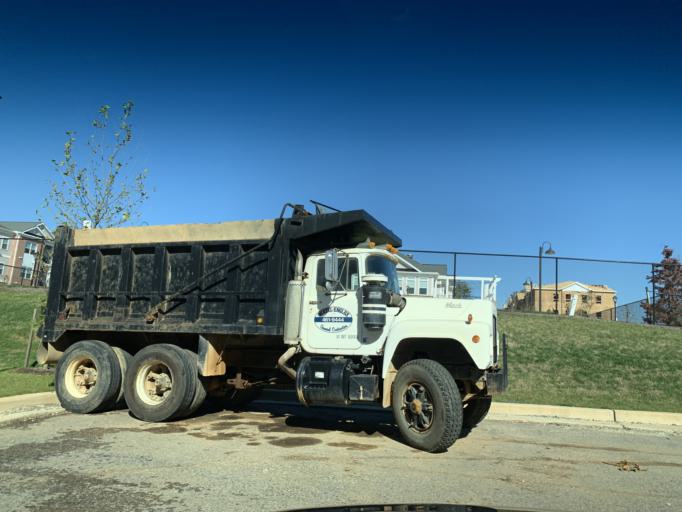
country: US
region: Maryland
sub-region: Baltimore County
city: White Marsh
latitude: 39.3849
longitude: -76.4381
